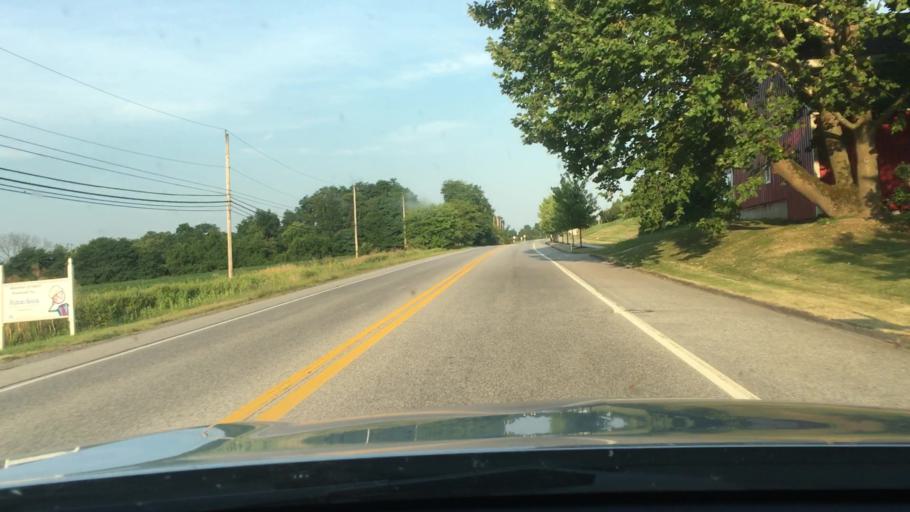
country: US
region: Pennsylvania
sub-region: York County
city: Dillsburg
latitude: 40.1070
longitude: -77.0287
